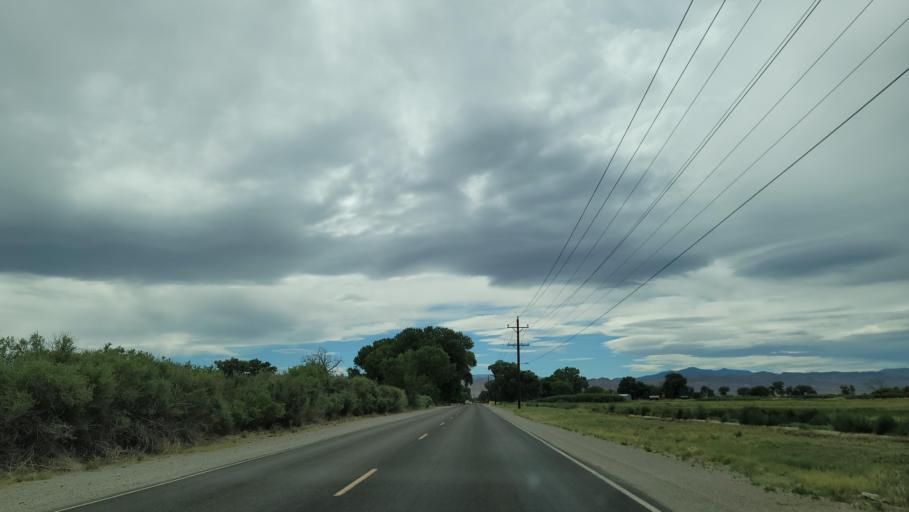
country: US
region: Nevada
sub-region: Lyon County
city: Yerington
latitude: 39.0482
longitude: -119.1504
